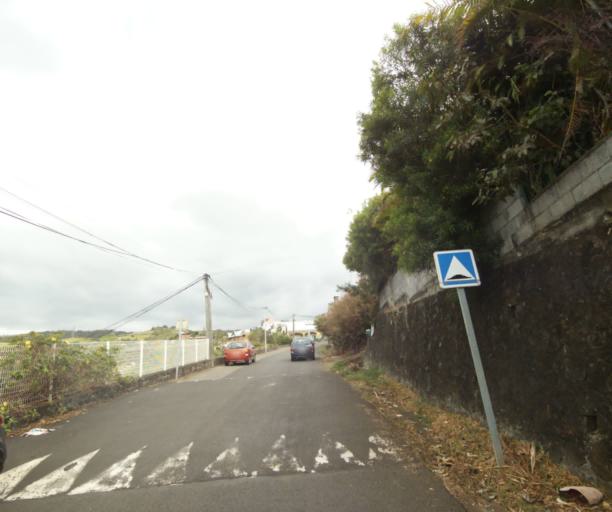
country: RE
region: Reunion
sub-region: Reunion
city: Saint-Paul
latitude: -21.0274
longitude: 55.3080
